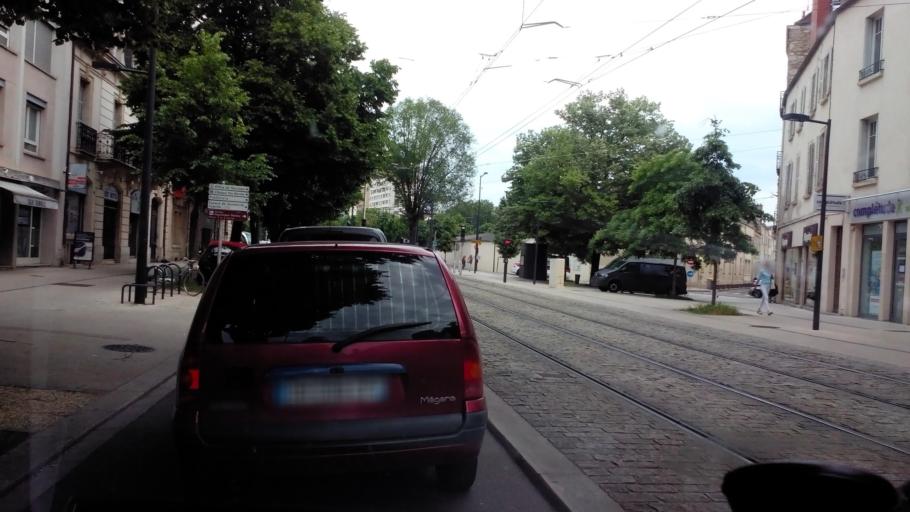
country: FR
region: Bourgogne
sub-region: Departement de la Cote-d'Or
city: Dijon
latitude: 47.3262
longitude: 5.0426
